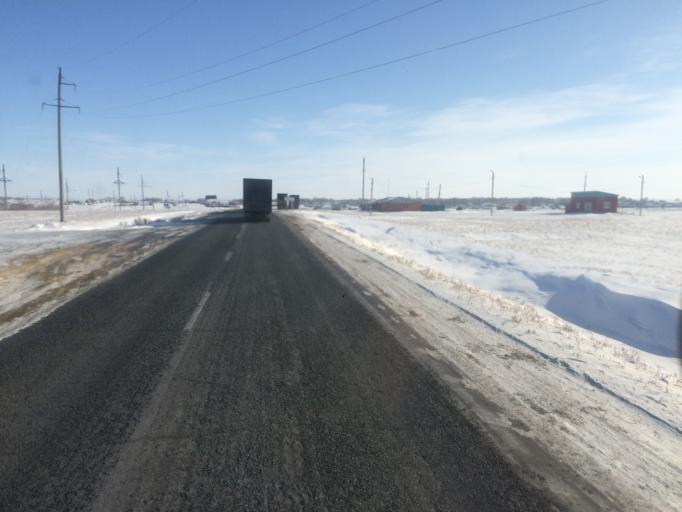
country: KZ
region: Aqtoebe
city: Khromtau
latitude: 50.1258
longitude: 59.0780
